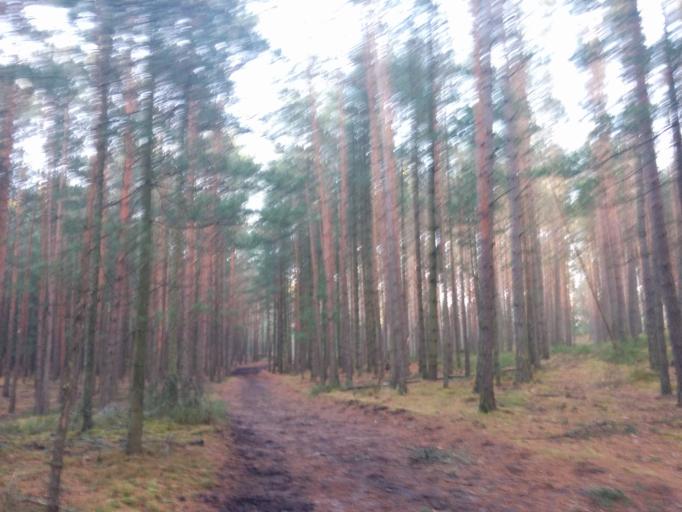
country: CZ
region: Central Bohemia
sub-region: Okres Mlada Boleslav
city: Zd'ar
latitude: 50.5235
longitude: 15.1210
